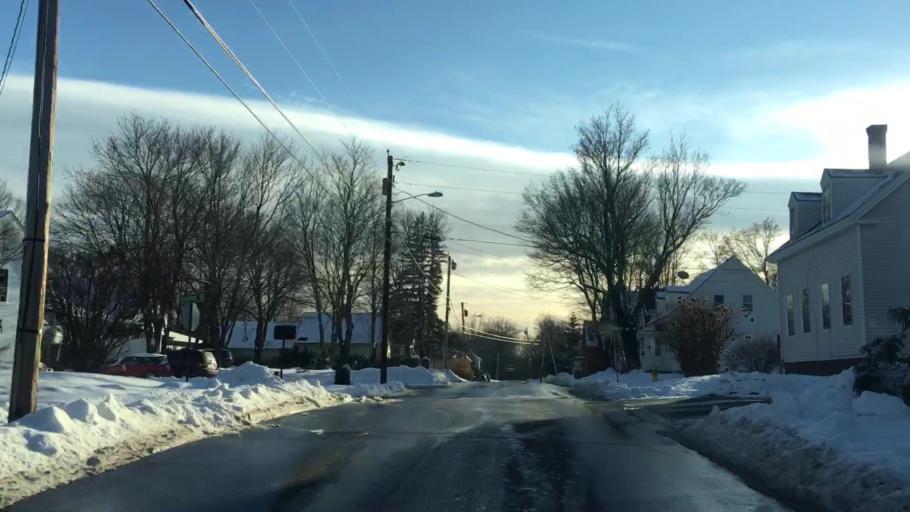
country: US
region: Maine
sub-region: Kennebec County
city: Gardiner
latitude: 44.2314
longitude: -69.7822
